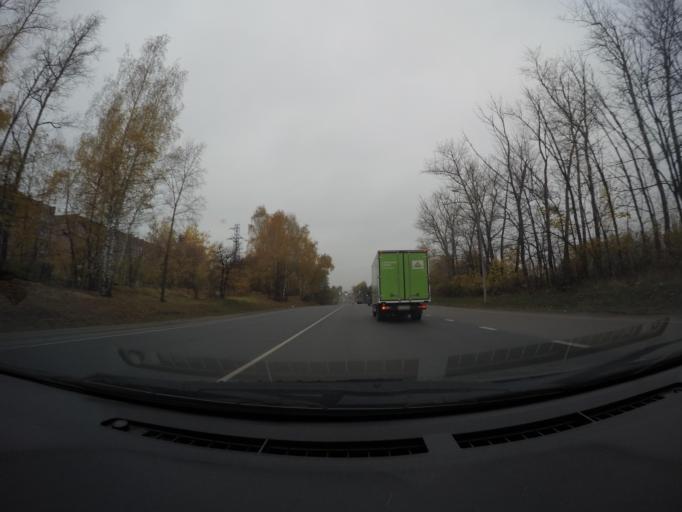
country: RU
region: Moskovskaya
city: Bronnitsy
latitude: 55.4145
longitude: 38.2636
